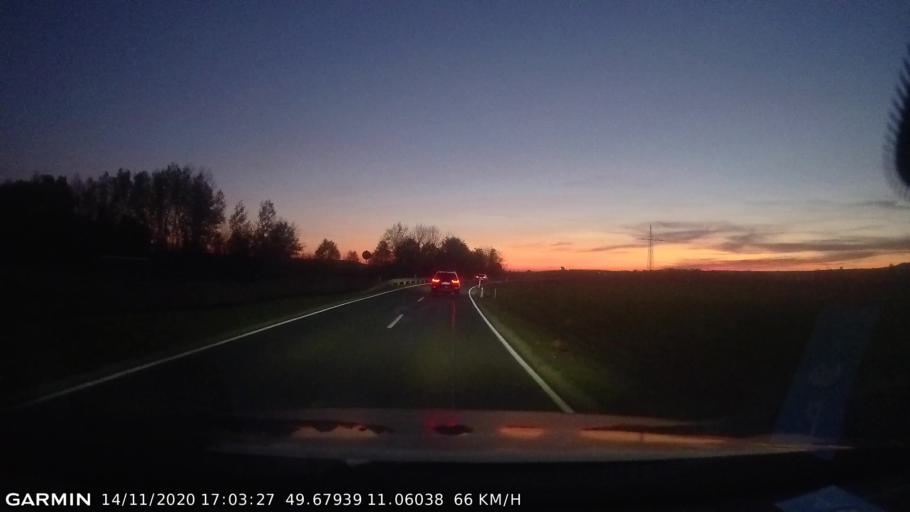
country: DE
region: Bavaria
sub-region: Upper Franconia
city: Poxdorf
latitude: 49.6793
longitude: 11.0605
